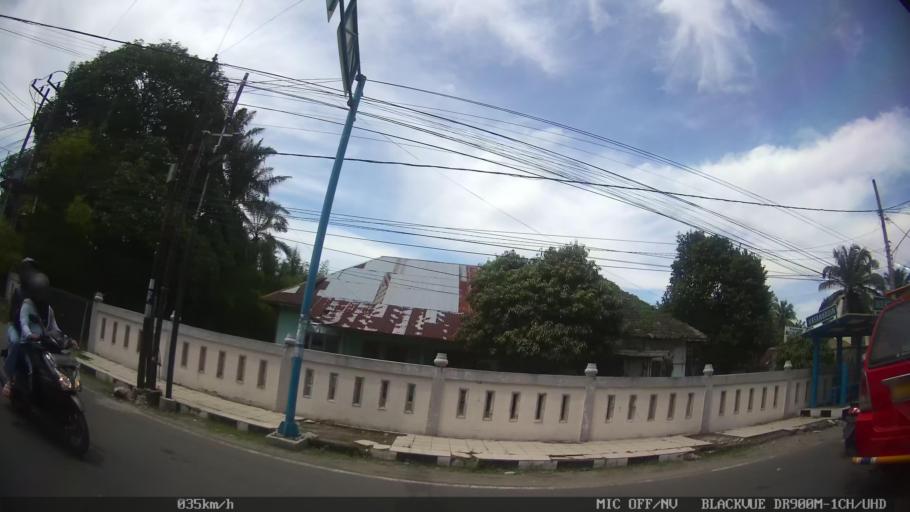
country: ID
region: North Sumatra
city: Binjai
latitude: 3.6014
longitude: 98.4843
